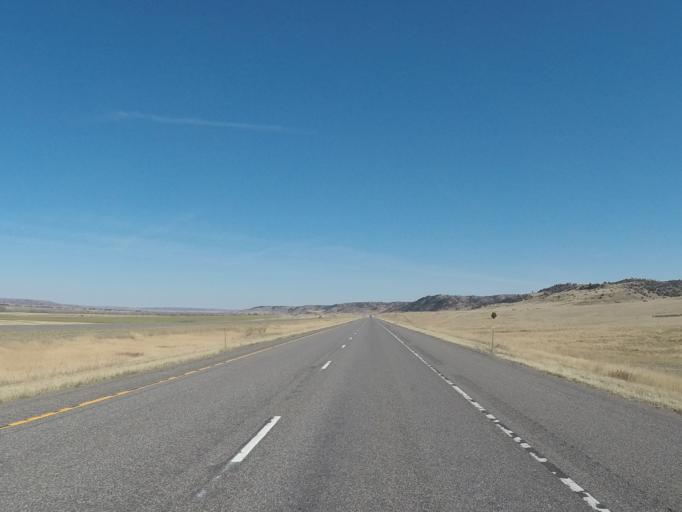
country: US
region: Montana
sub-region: Sweet Grass County
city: Big Timber
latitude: 45.7566
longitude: -110.1317
